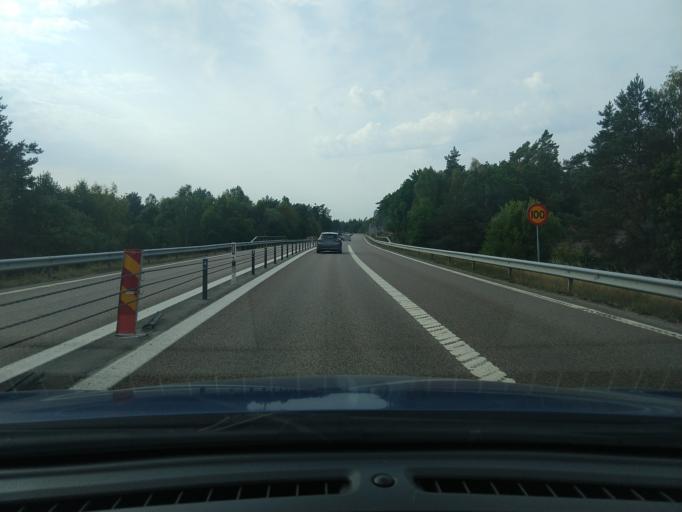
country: SE
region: Blekinge
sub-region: Ronneby Kommun
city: Kallinge
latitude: 56.2081
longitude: 15.3252
